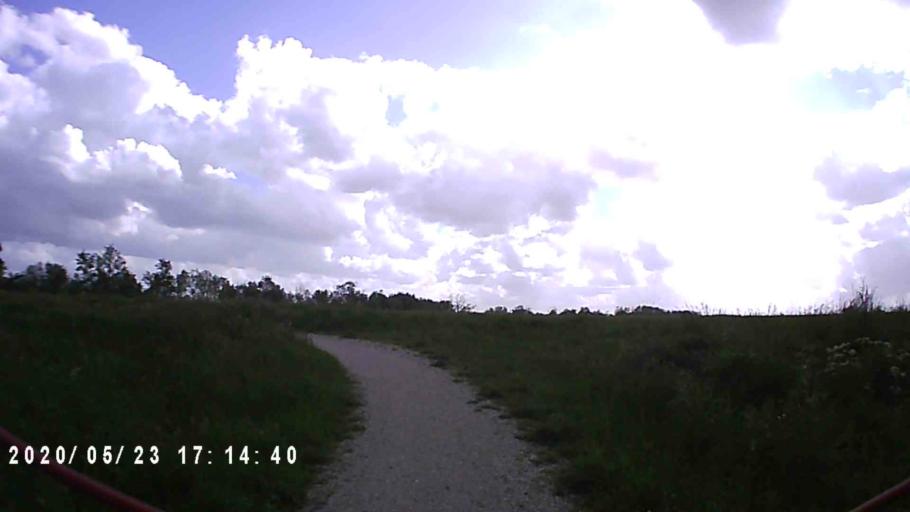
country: NL
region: Groningen
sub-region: Gemeente Slochteren
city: Slochteren
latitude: 53.2637
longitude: 6.8048
